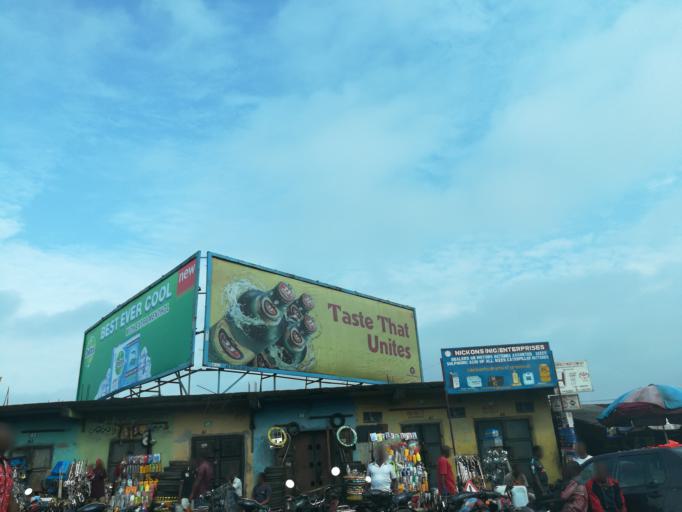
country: NG
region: Rivers
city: Port Harcourt
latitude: 4.7990
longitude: 6.9931
